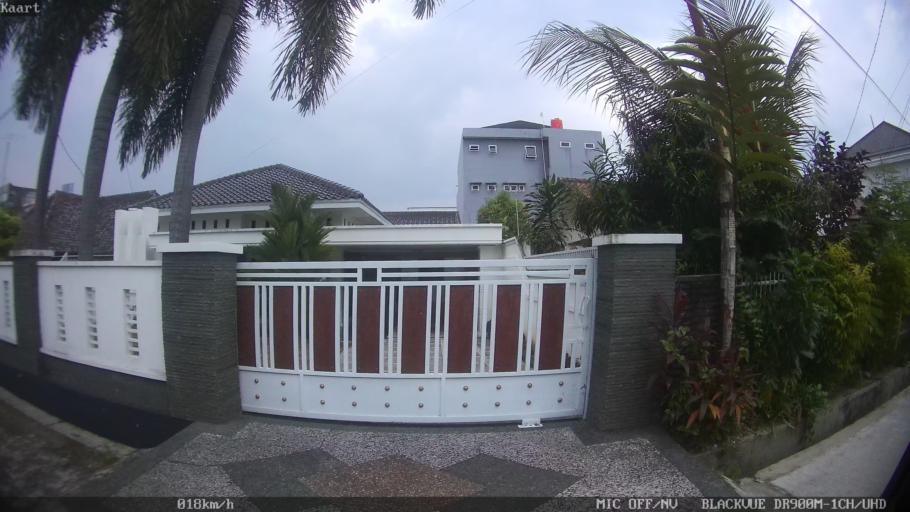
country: ID
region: Lampung
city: Bandarlampung
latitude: -5.4233
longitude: 105.2655
